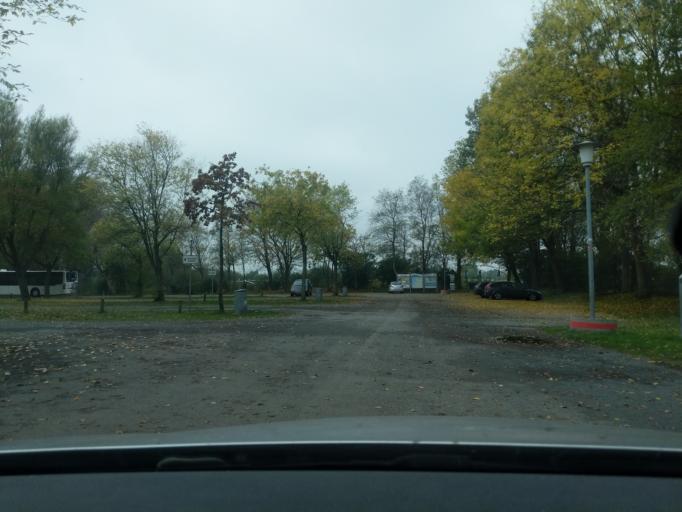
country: DE
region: Lower Saxony
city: Otterndorf
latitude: 53.8229
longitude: 8.8821
